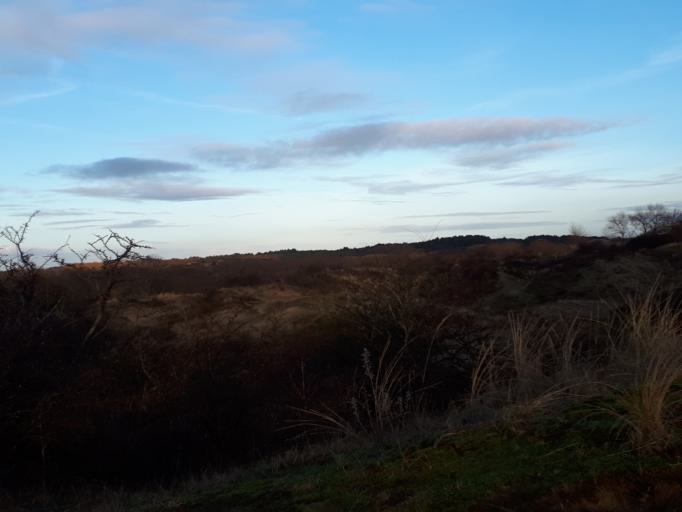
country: NL
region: South Holland
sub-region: Gemeente Wassenaar
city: Wassenaar
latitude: 52.1380
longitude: 4.3561
